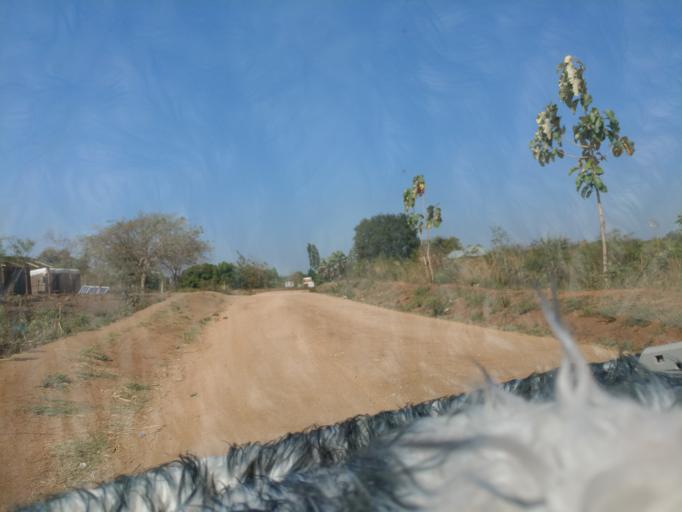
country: UG
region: Northern Region
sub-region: Yumbe District
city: Yumbe
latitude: 3.3877
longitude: 31.3594
